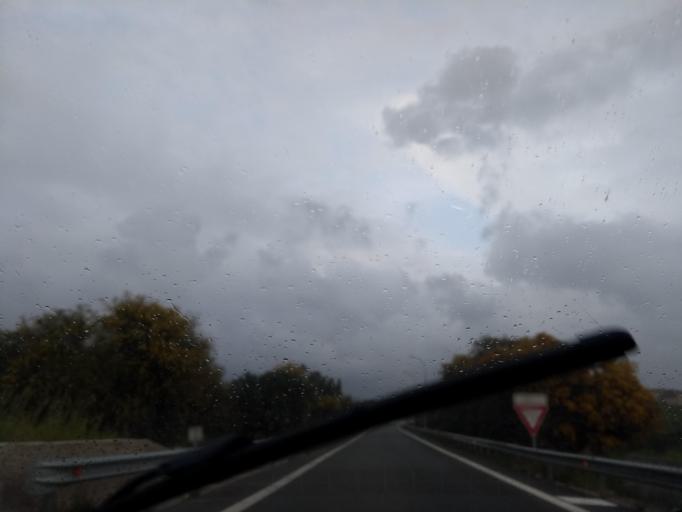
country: IT
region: Sicily
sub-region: Trapani
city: Fulgatore-Torretta
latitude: 37.9623
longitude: 12.6287
